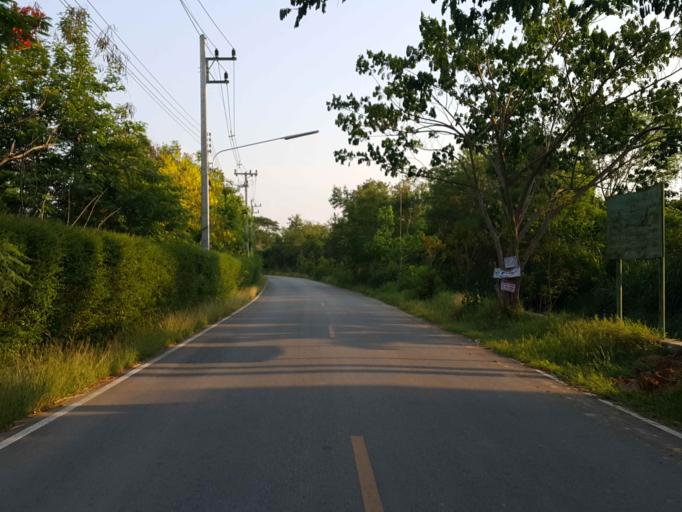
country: TH
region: Chiang Mai
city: Saraphi
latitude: 18.7190
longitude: 98.9798
